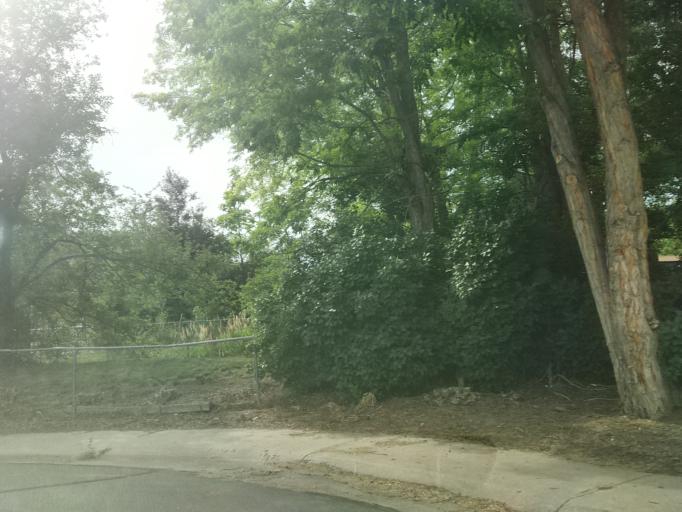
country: US
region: Colorado
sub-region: Jefferson County
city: Lakewood
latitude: 39.7009
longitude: -105.1044
